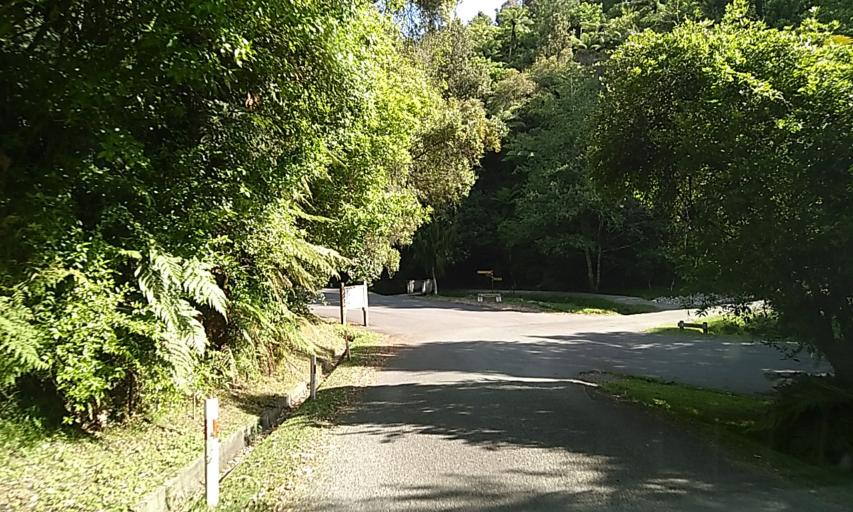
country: NZ
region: Bay of Plenty
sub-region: Tauranga City
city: Tauranga
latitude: -37.8135
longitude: 176.0462
